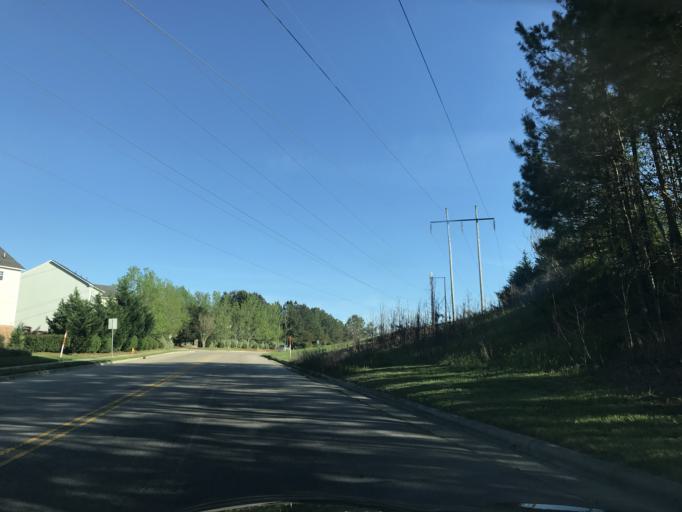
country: US
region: North Carolina
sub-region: Wake County
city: Raleigh
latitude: 35.8415
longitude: -78.5669
